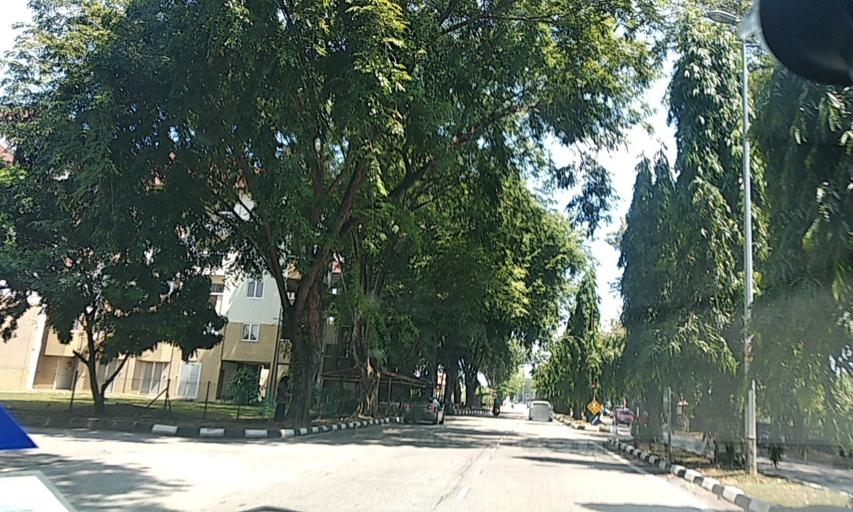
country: MY
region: Kedah
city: Sungai Petani
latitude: 5.6350
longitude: 100.4779
